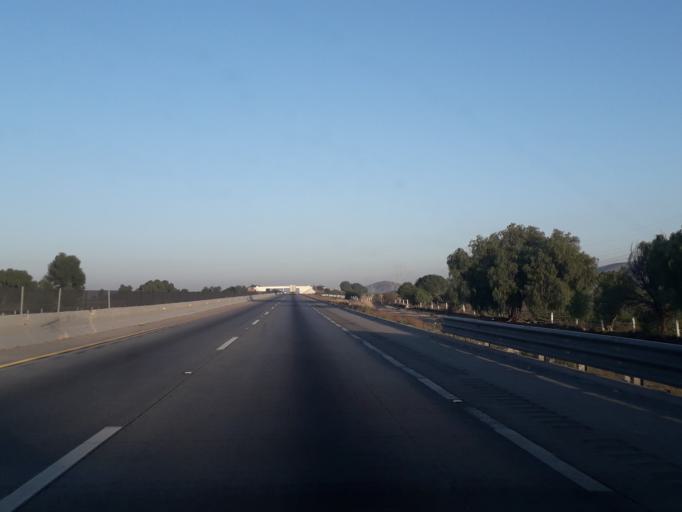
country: MX
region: Puebla
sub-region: Tepeaca
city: San Cristobal los Nava
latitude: 18.9848
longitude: -97.8343
